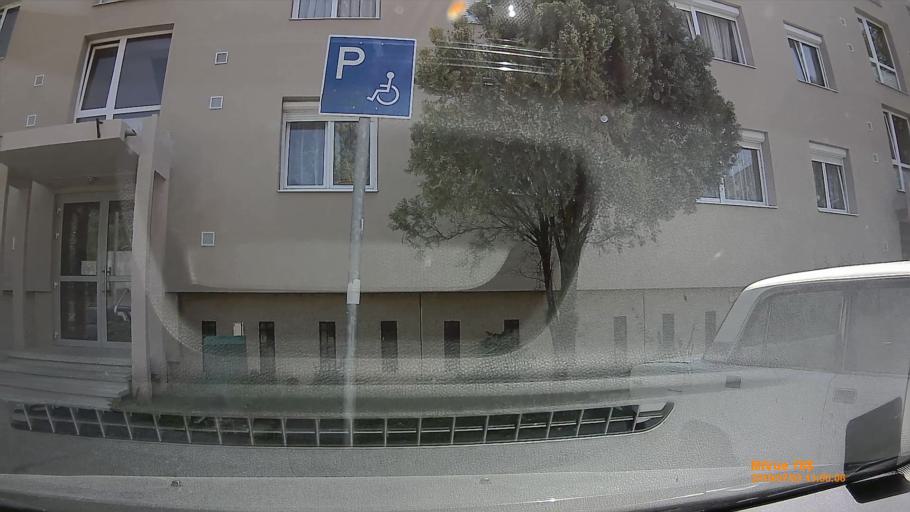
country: HU
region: Gyor-Moson-Sopron
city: Gyor
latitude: 47.6777
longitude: 17.6431
